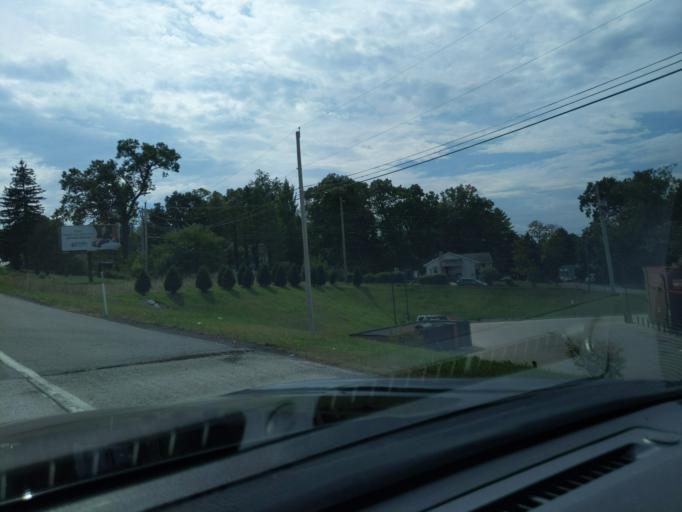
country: US
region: Pennsylvania
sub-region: Blair County
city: Lakemont
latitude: 40.4770
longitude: -78.3903
